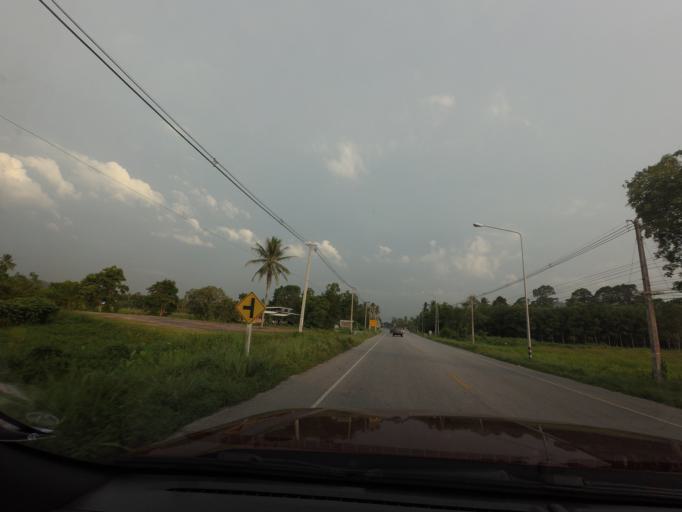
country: TH
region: Pattani
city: Mae Lan
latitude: 6.6243
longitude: 101.1882
